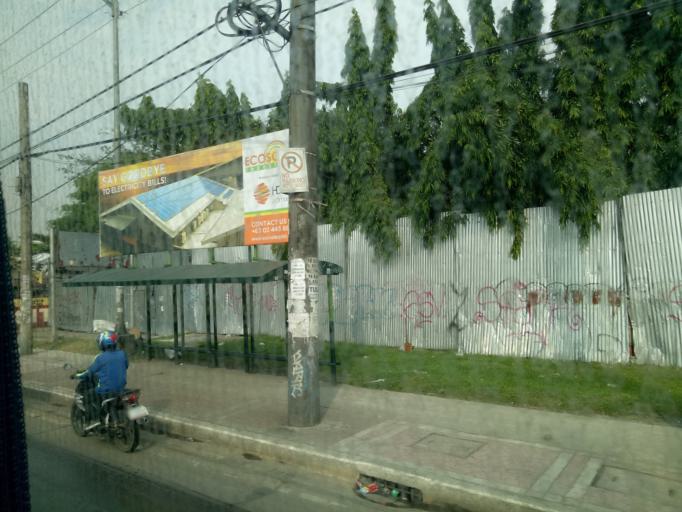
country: PH
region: Calabarzon
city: Bagong Pagasa
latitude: 14.7113
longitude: 121.0396
